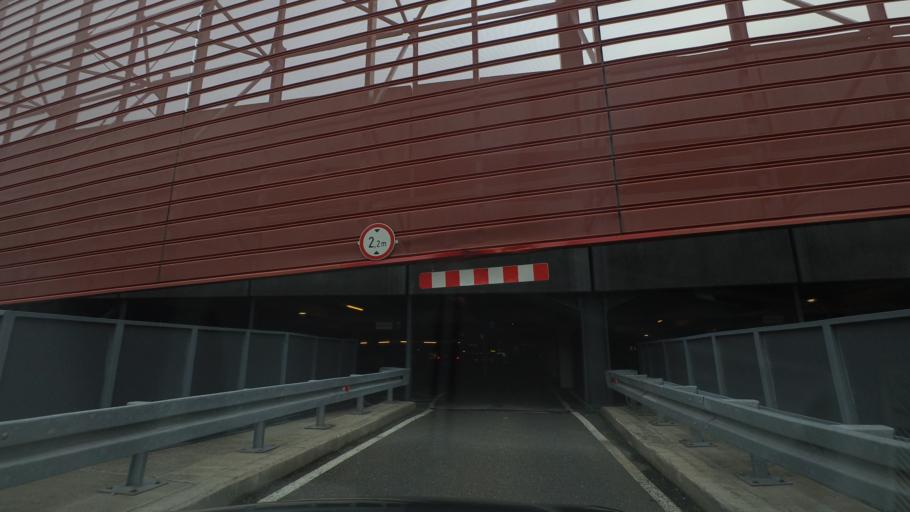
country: HR
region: Zagrebacka
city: Jablanovec
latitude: 45.8719
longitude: 15.8291
